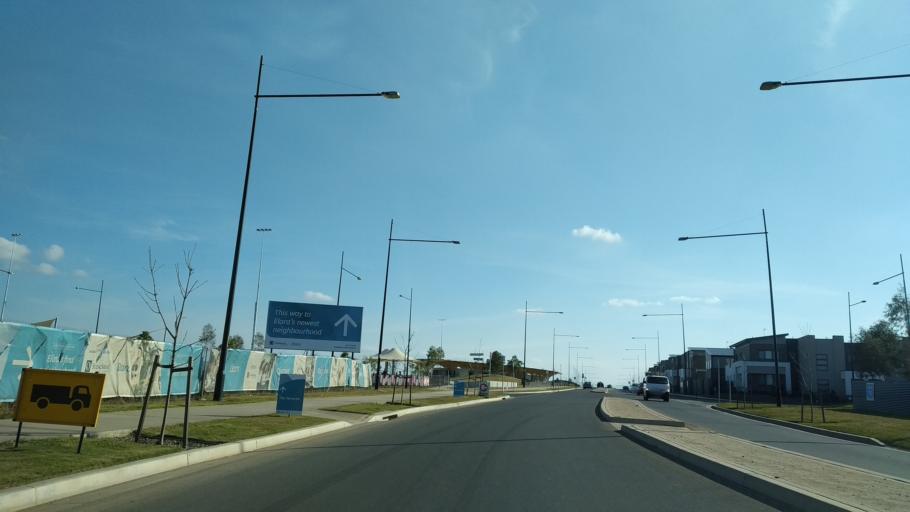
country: AU
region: New South Wales
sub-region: Blacktown
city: Hassall Grove
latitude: -33.6951
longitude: 150.8198
